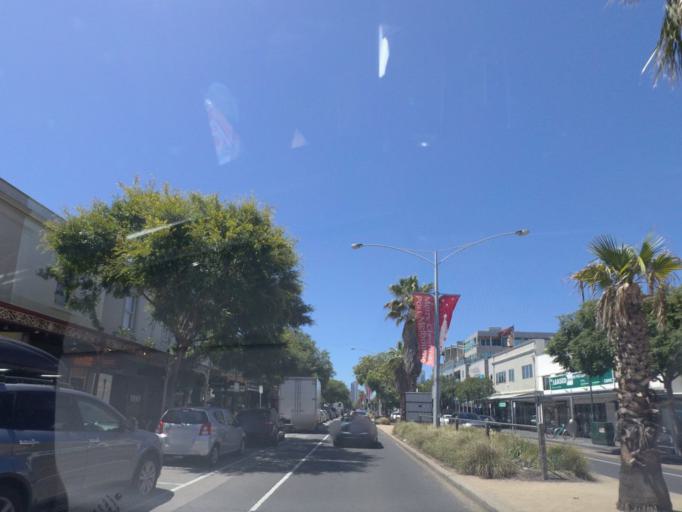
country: AU
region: Victoria
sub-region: Port Phillip
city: Port Melbourne
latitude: -37.8397
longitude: 144.9412
